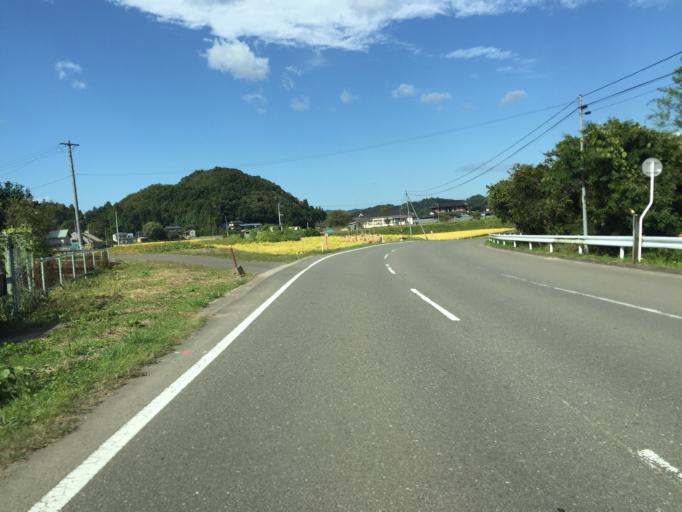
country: JP
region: Fukushima
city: Yanagawamachi-saiwaicho
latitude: 37.8288
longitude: 140.6127
